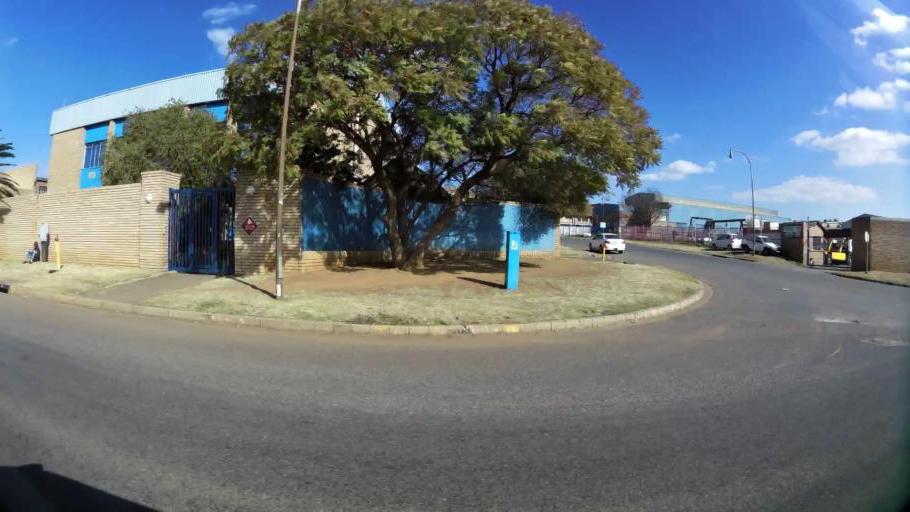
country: ZA
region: Gauteng
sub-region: City of Johannesburg Metropolitan Municipality
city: Soweto
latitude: -26.2710
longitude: 27.9368
